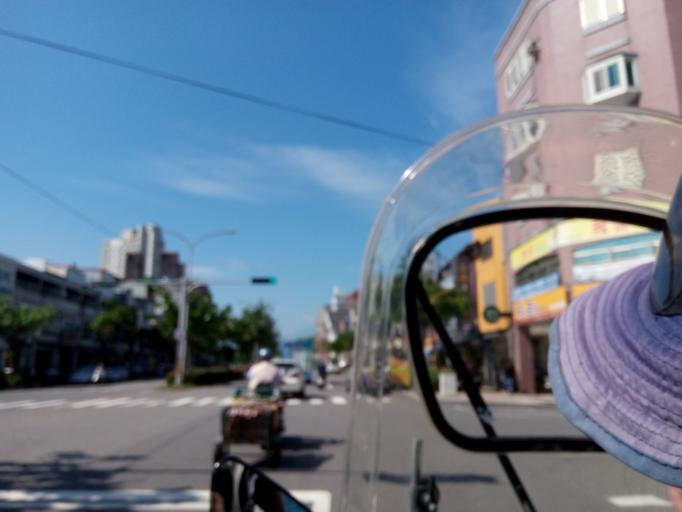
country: TW
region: Taiwan
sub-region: Yilan
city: Yilan
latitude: 24.6808
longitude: 121.7604
